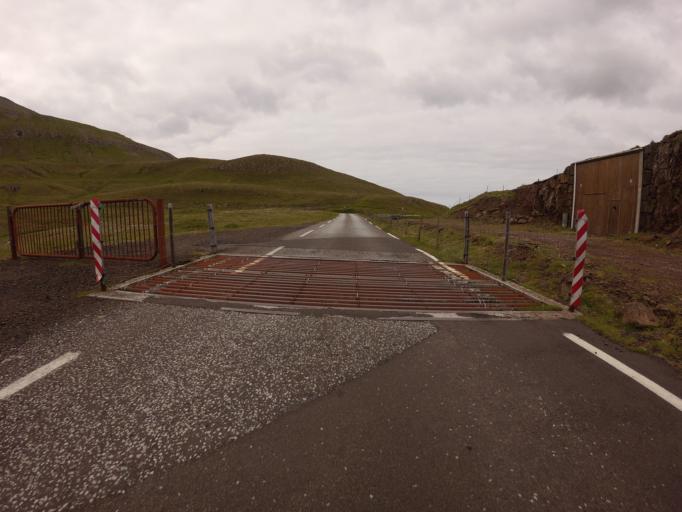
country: FO
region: Suduroy
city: Tvoroyri
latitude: 61.5169
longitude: -6.8733
